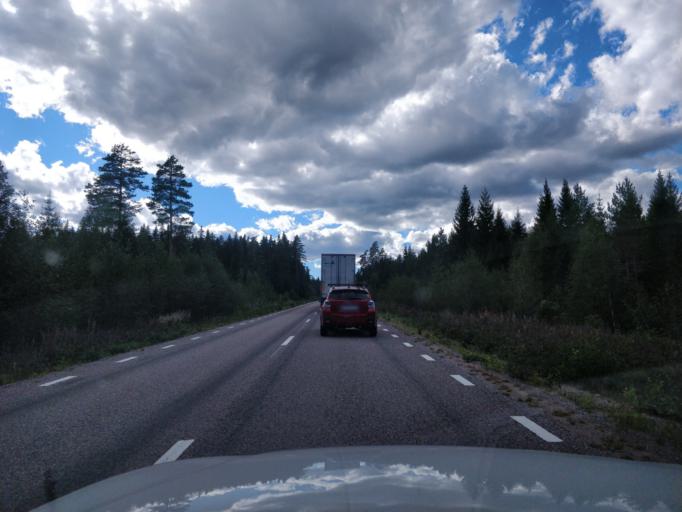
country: SE
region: Dalarna
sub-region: Ludvika Kommun
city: Abborrberget
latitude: 60.1866
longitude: 14.7822
